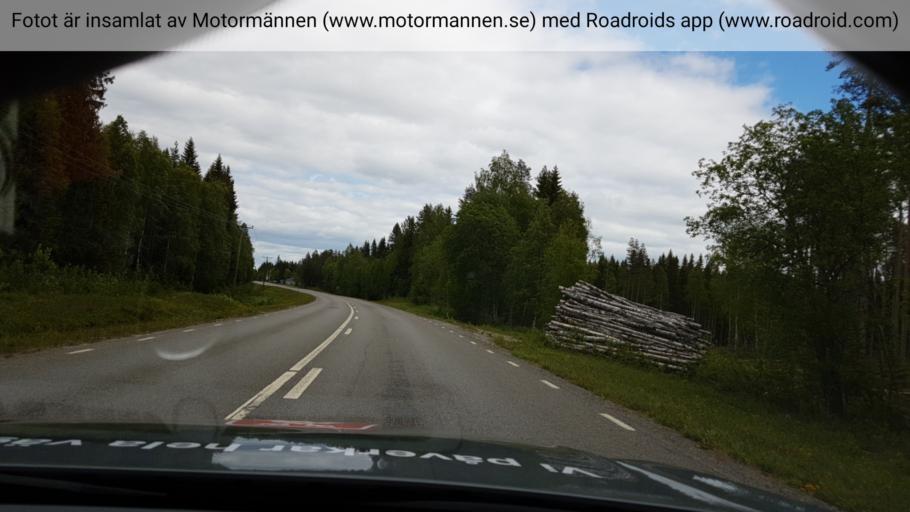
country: SE
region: Jaemtland
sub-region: Stroemsunds Kommun
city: Stroemsund
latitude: 64.3106
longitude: 15.2212
